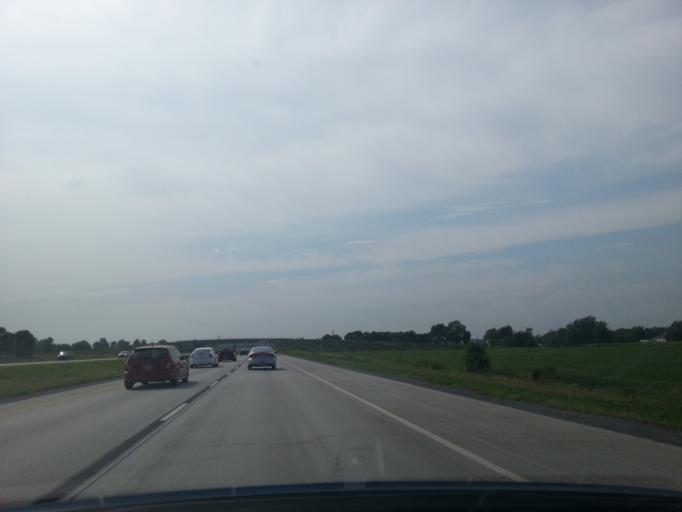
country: CA
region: Quebec
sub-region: Monteregie
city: Saint-Constant
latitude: 45.3640
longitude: -73.5956
